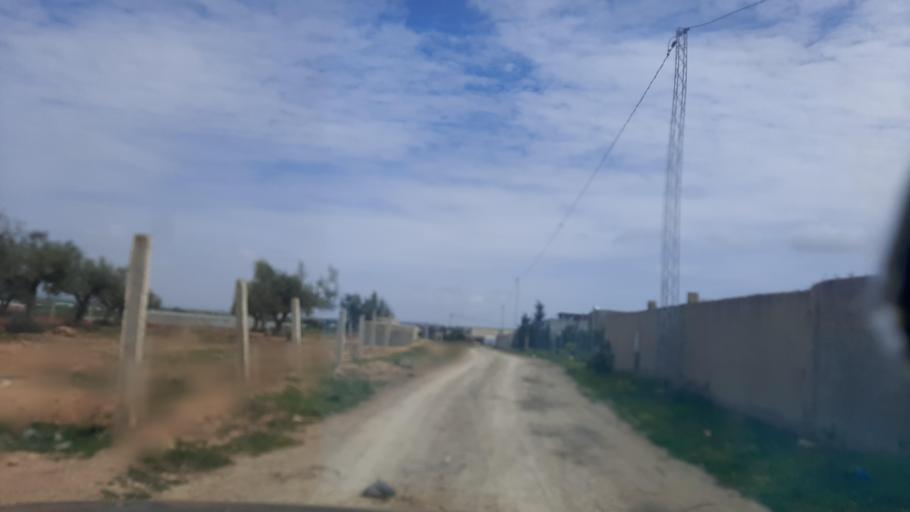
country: TN
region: Tunis
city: Oued Lill
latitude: 36.6926
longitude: 9.9958
